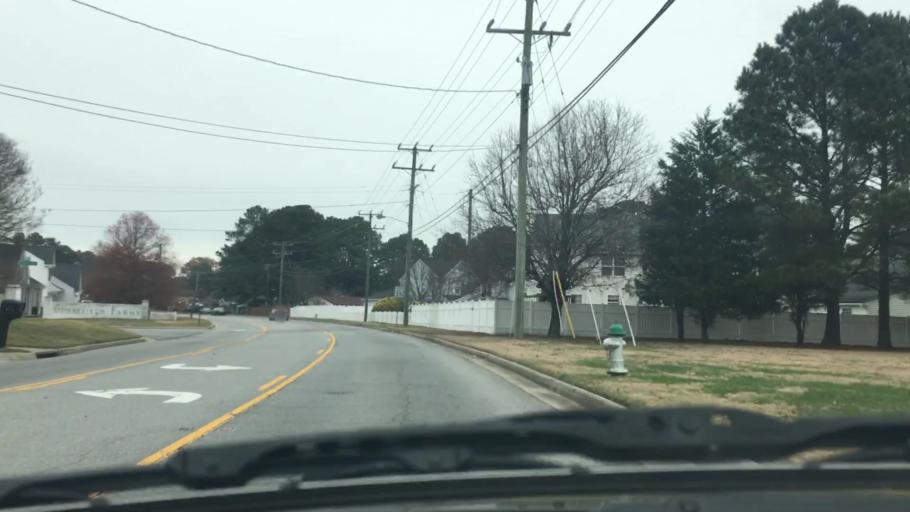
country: US
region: Virginia
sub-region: City of Portsmouth
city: Portsmouth Heights
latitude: 36.8599
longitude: -76.3769
